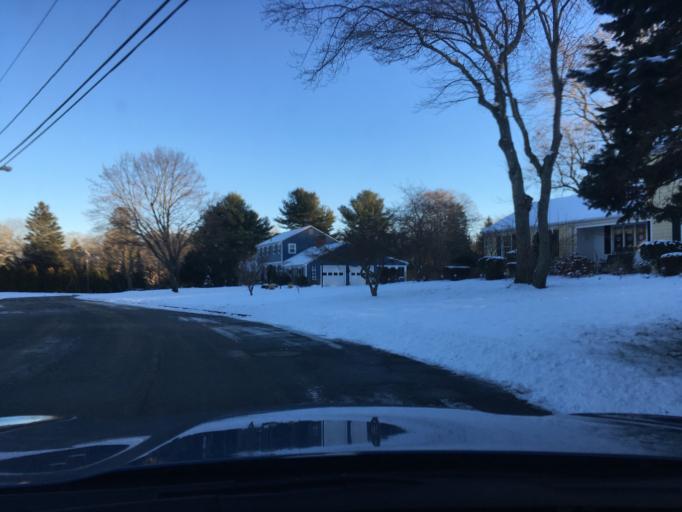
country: US
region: Rhode Island
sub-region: Kent County
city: East Greenwich
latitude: 41.6521
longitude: -71.4727
